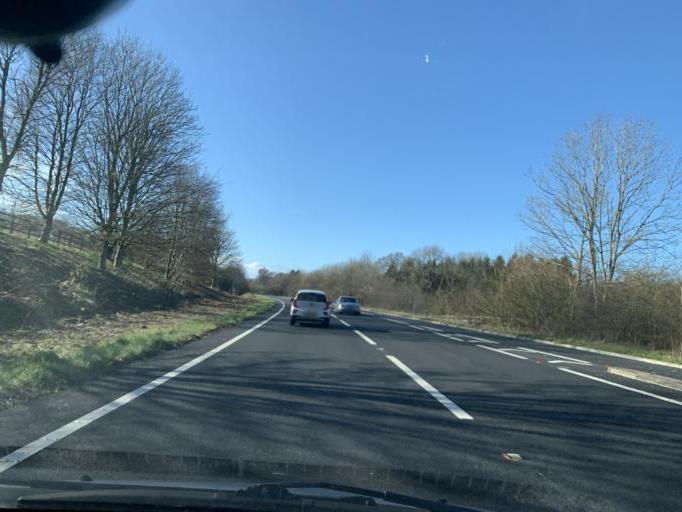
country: GB
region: England
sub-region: Wiltshire
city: Bishopstrow
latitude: 51.1850
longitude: -2.1372
